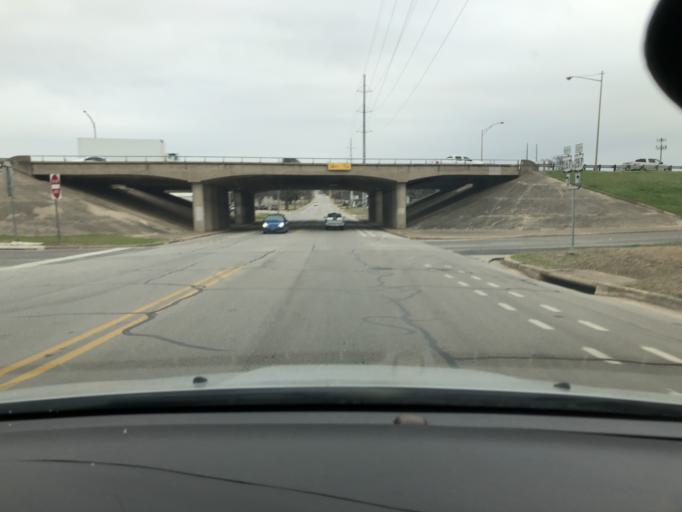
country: US
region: Texas
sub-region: Tarrant County
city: Fort Worth
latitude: 32.7267
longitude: -97.2989
